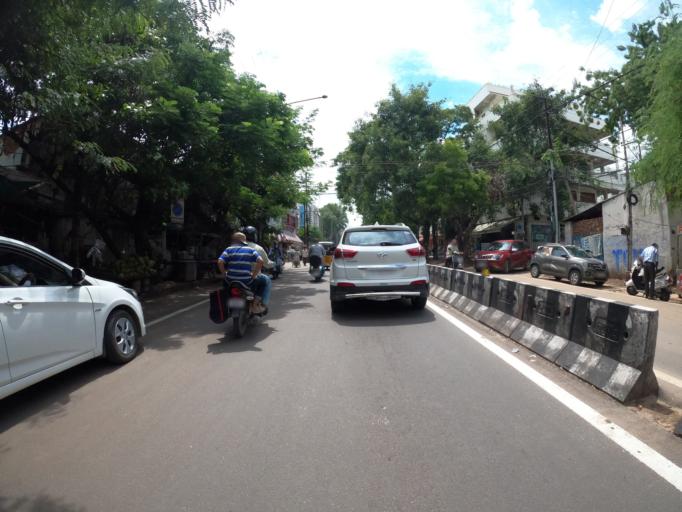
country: IN
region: Telangana
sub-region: Hyderabad
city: Hyderabad
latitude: 17.3998
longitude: 78.4790
